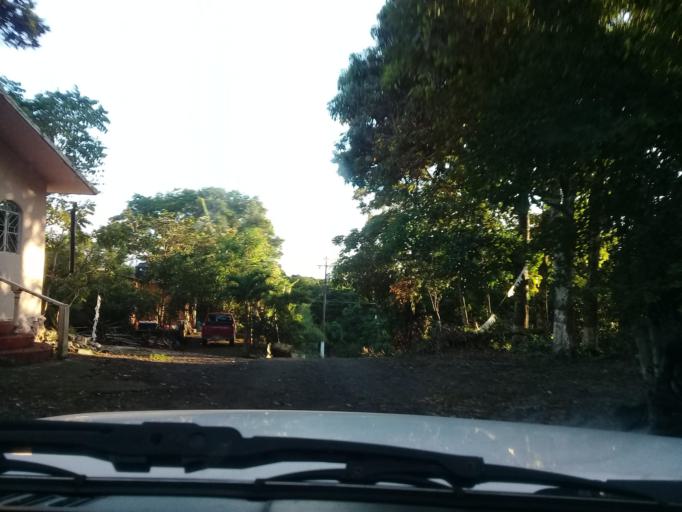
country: MX
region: Veracruz
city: Catemaco
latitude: 18.4319
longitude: -95.0896
